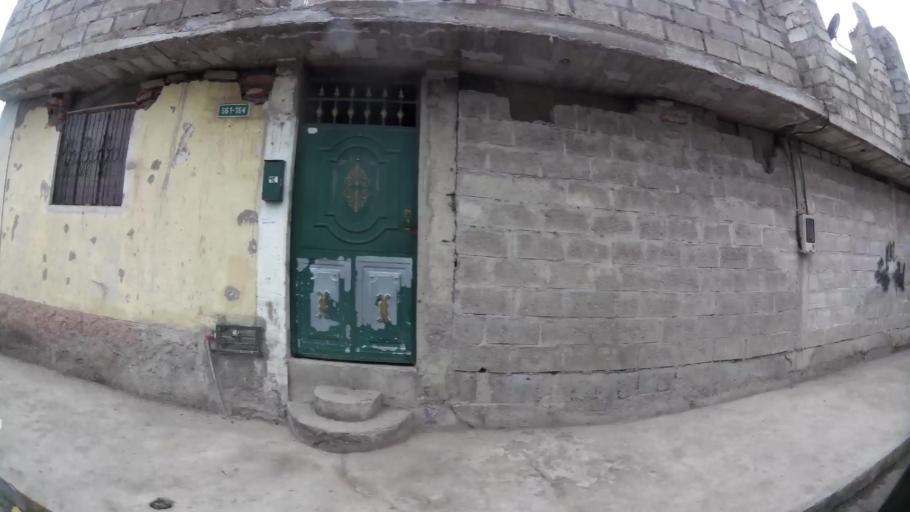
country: EC
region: Pichincha
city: Sangolqui
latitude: -0.3483
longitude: -78.5555
